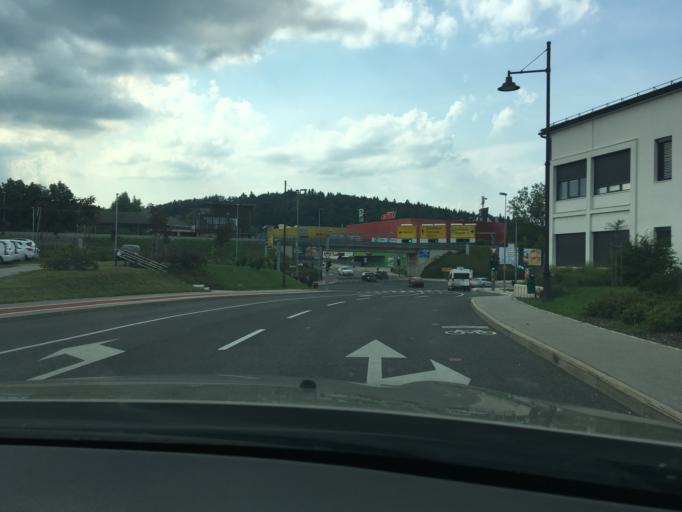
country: SI
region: Novo Mesto
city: Novo Mesto
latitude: 45.8018
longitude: 15.1627
